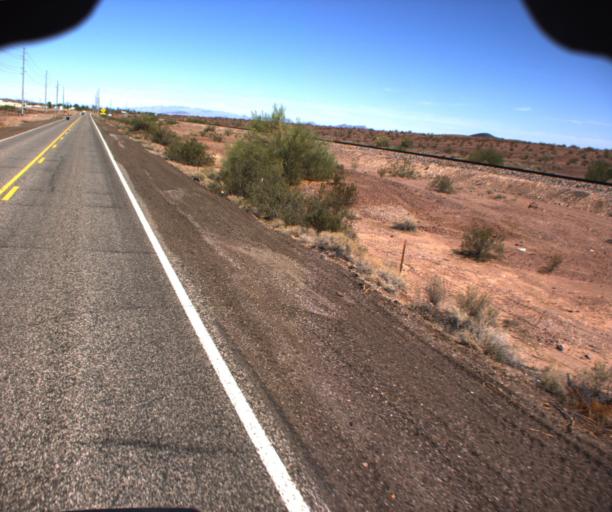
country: US
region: Arizona
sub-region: La Paz County
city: Quartzsite
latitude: 33.9084
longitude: -113.9841
